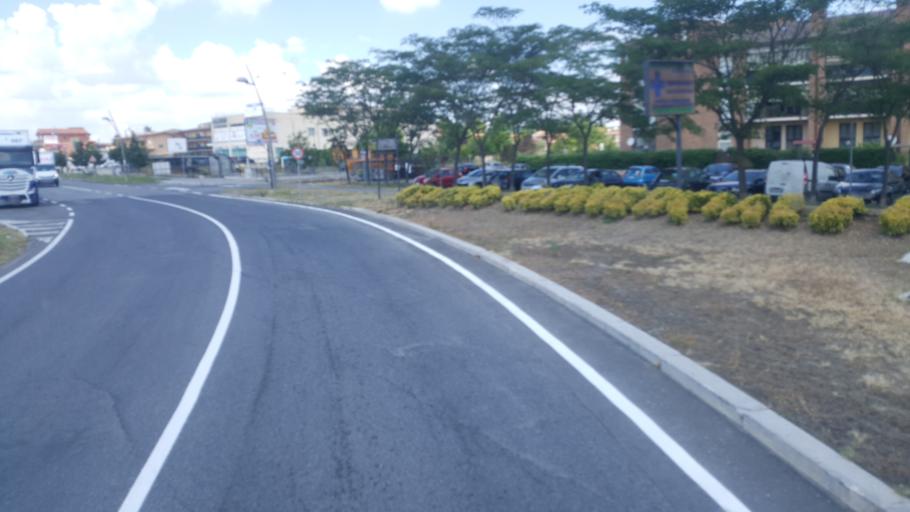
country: IT
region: Latium
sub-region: Citta metropolitana di Roma Capitale
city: Fiano Romano
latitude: 42.1403
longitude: 12.5998
